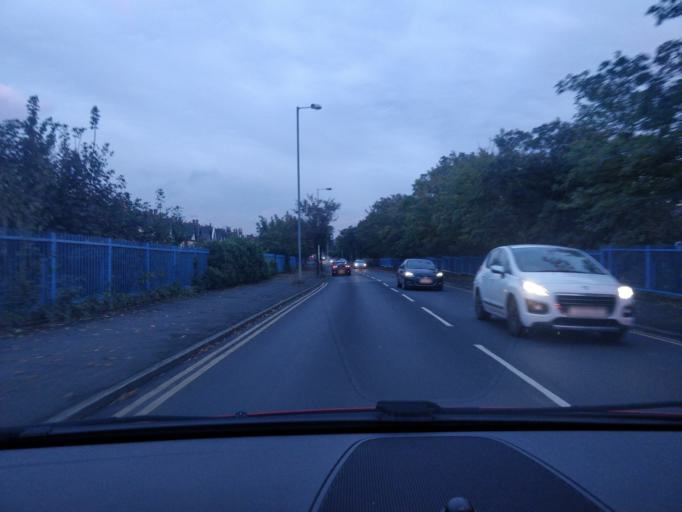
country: GB
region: England
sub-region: Sefton
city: Southport
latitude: 53.6464
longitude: -2.9763
